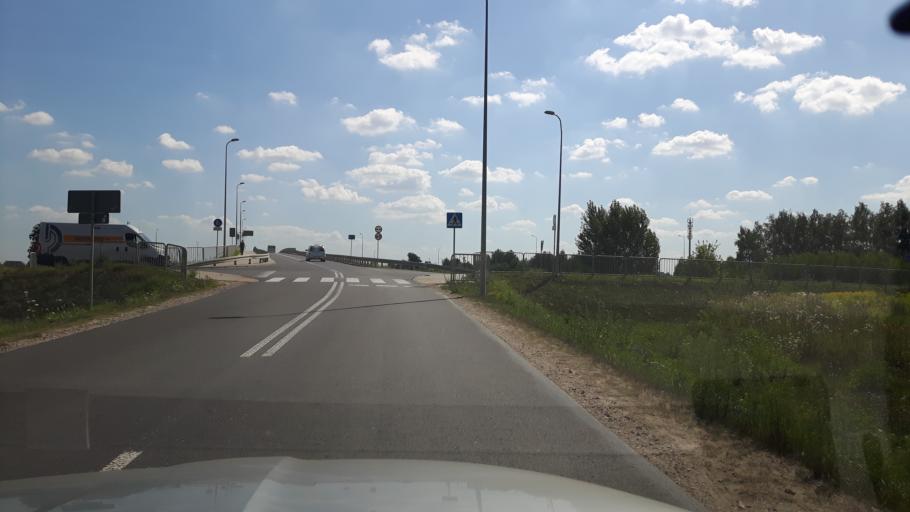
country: PL
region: Masovian Voivodeship
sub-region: Powiat pruszkowski
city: Michalowice
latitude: 52.1297
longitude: 20.8742
